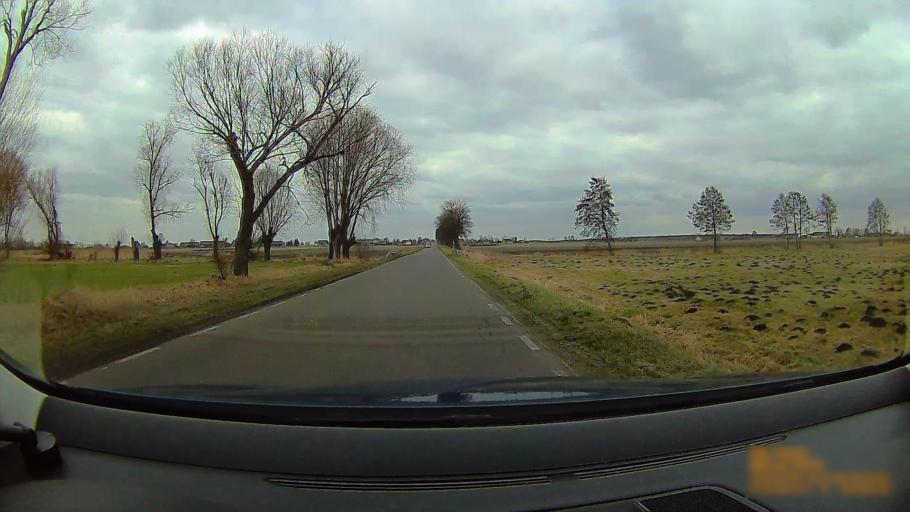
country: PL
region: Greater Poland Voivodeship
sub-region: Powiat koninski
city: Rychwal
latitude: 52.1001
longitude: 18.1015
